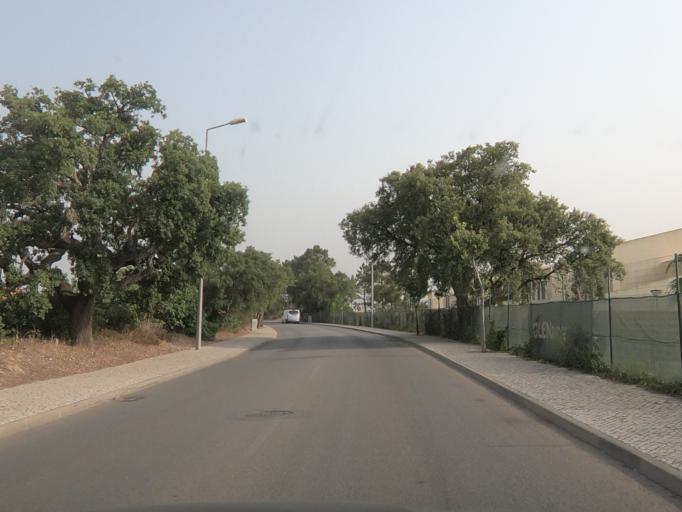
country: PT
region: Faro
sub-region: Albufeira
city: Guia
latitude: 37.0883
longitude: -8.3102
